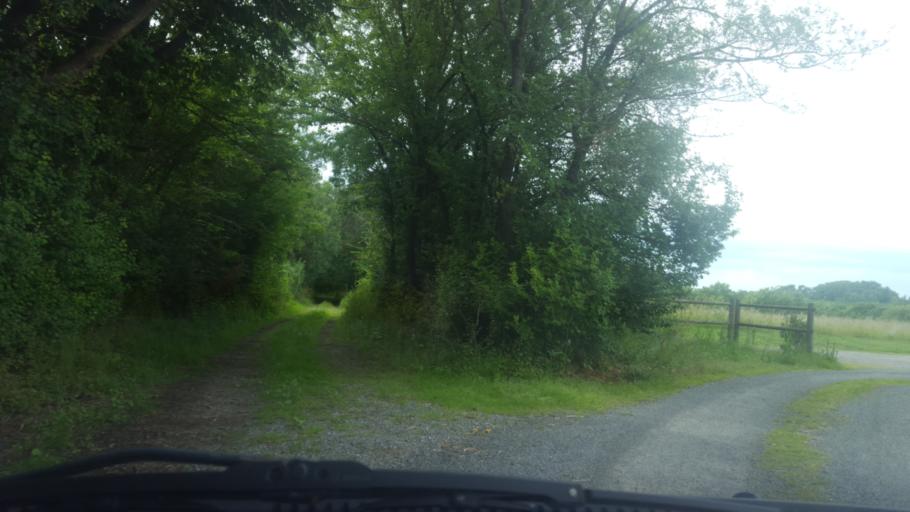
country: FR
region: Pays de la Loire
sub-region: Departement de la Loire-Atlantique
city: La Limouziniere
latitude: 47.0262
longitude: -1.6054
